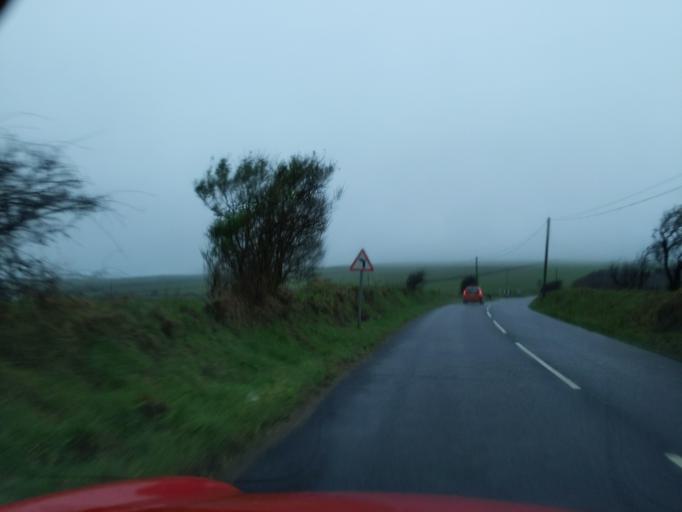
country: GB
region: England
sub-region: Cornwall
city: Camelford
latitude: 50.6451
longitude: -4.6973
